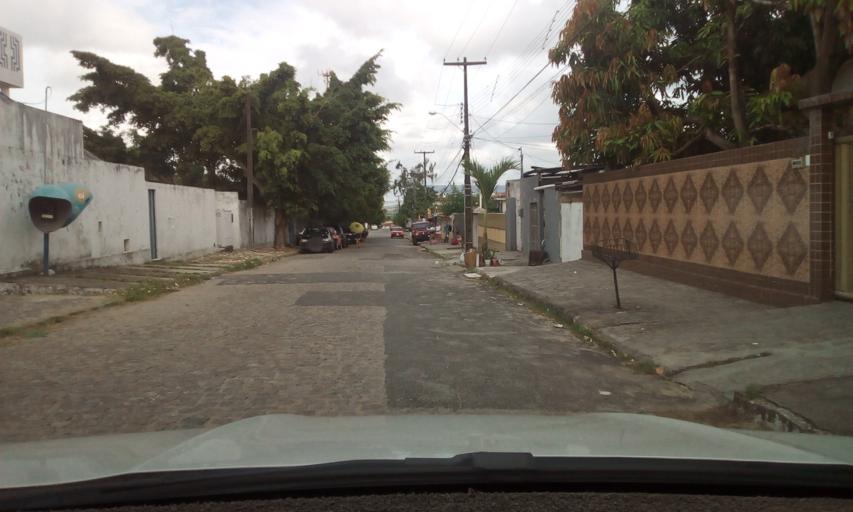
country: BR
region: Paraiba
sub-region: Joao Pessoa
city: Joao Pessoa
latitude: -7.1106
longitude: -34.8668
